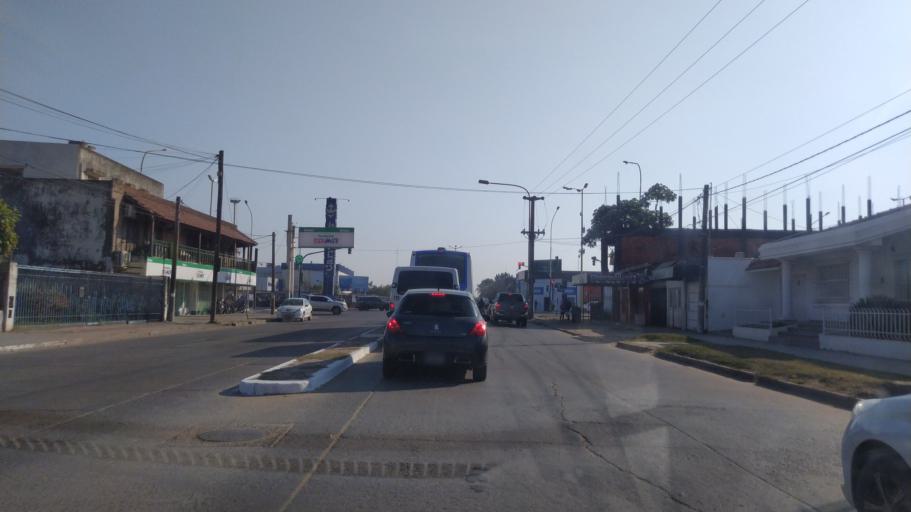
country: AR
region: Corrientes
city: Corrientes
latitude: -27.4792
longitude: -58.8149
